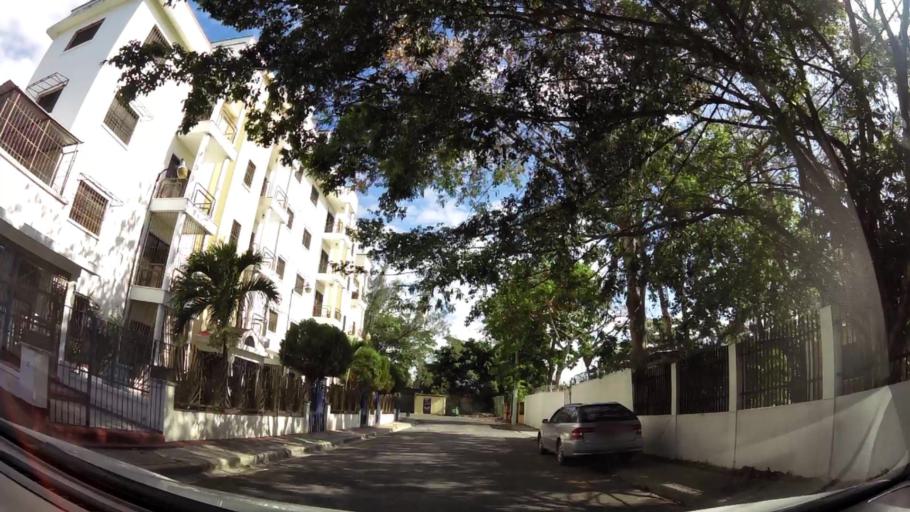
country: DO
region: Santo Domingo
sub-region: Santo Domingo
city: Boca Chica
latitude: 18.4535
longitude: -69.6067
